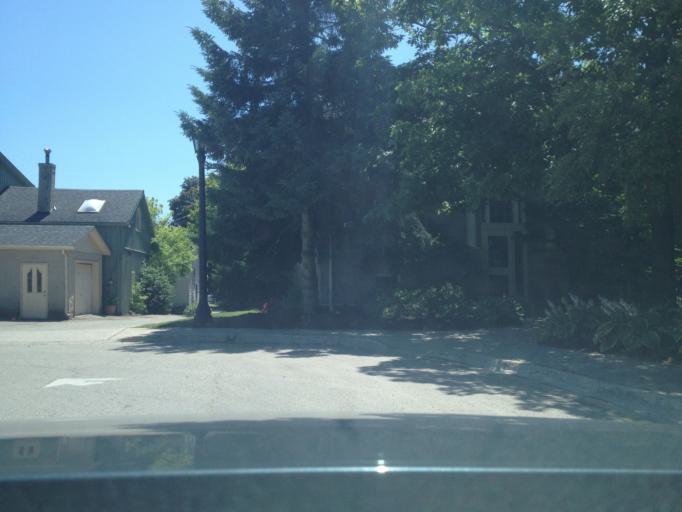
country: CA
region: Ontario
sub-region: Wellington County
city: Guelph
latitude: 43.6831
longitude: -80.4312
